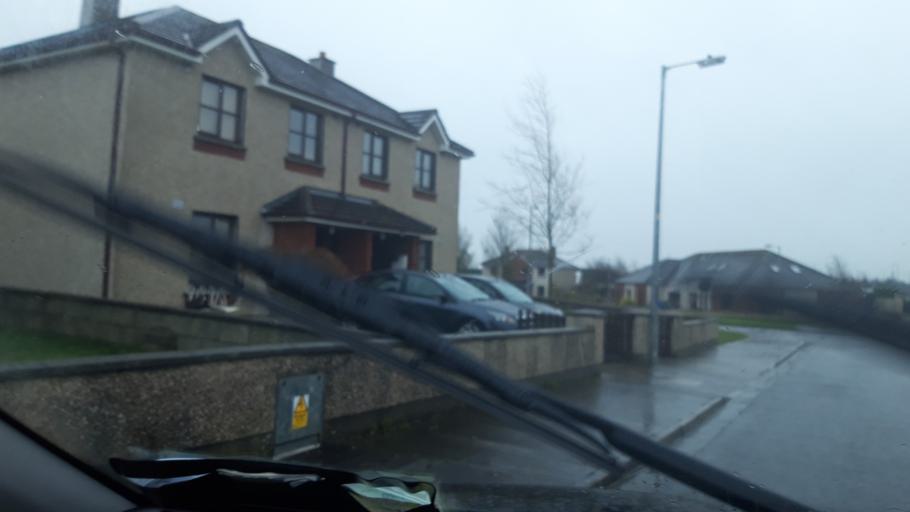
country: IE
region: Leinster
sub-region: Kilkenny
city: Kilkenny
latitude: 52.6598
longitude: -7.2282
